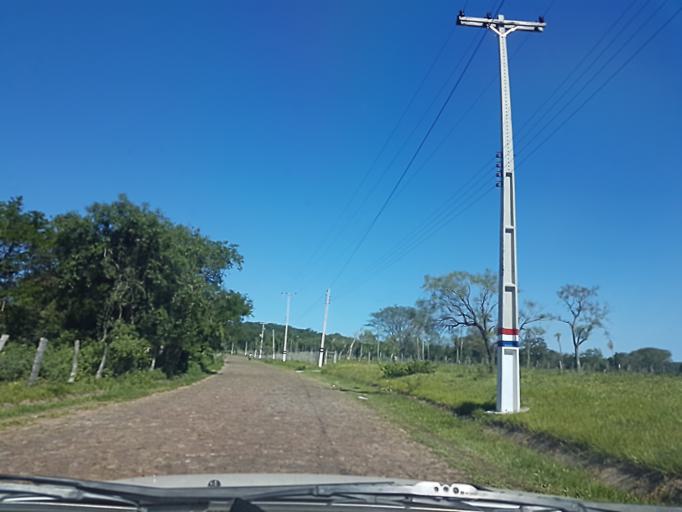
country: PY
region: Cordillera
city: Atyra
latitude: -25.2786
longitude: -57.1630
